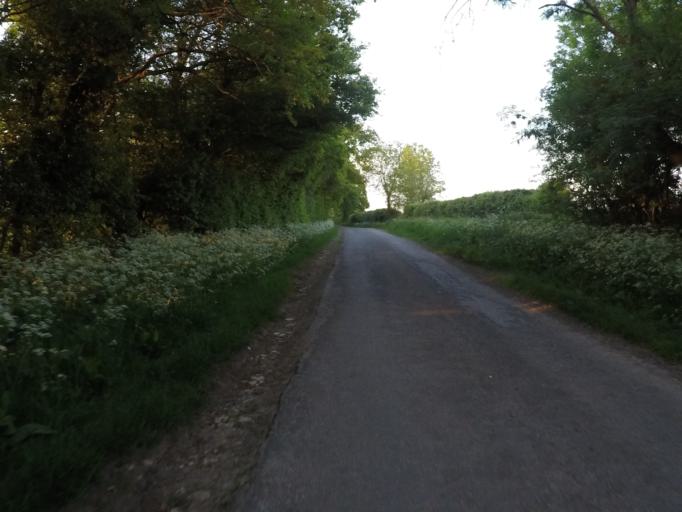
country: GB
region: England
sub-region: Oxfordshire
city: North Leigh
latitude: 51.8298
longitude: -1.4759
